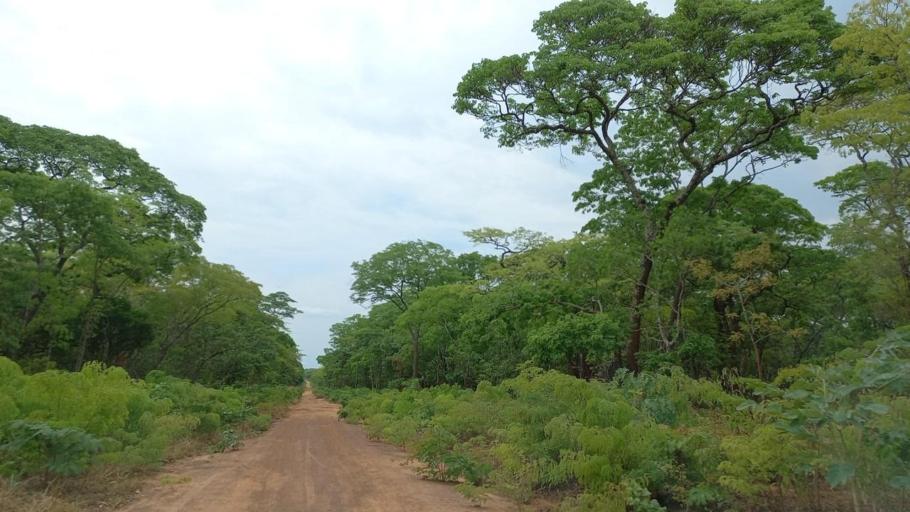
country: ZM
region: North-Western
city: Kalengwa
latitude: -13.5818
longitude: 24.9714
